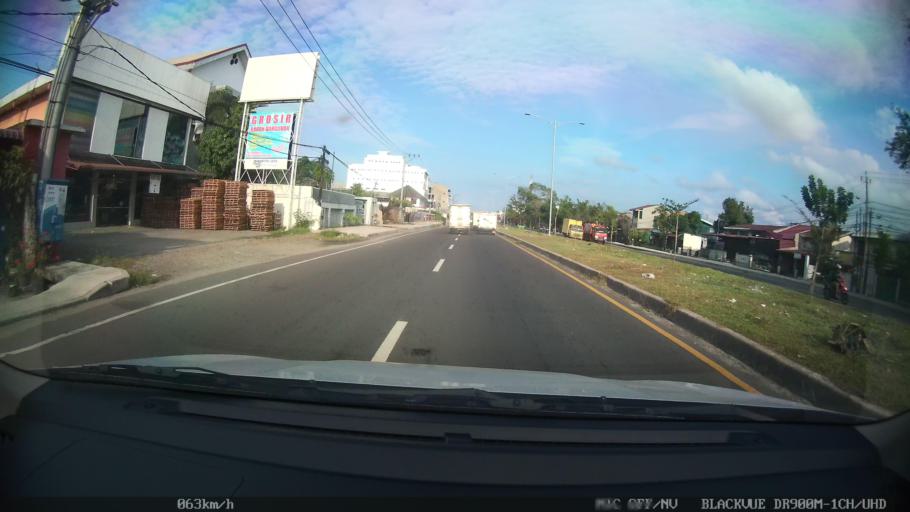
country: ID
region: North Sumatra
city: Medan
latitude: 3.6157
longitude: 98.6396
